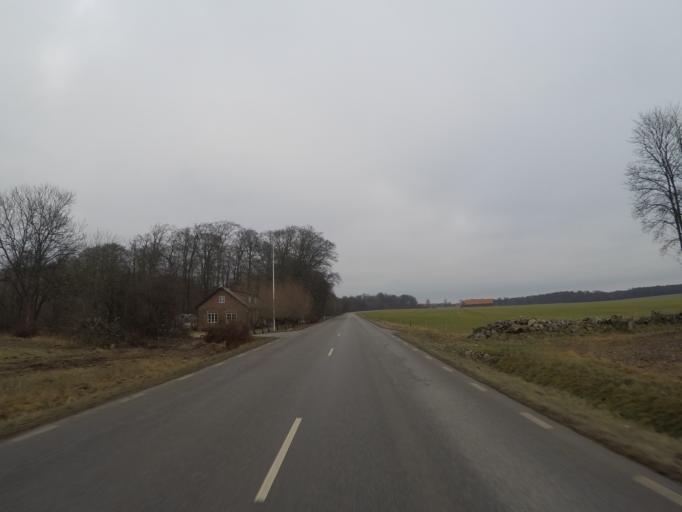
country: SE
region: Skane
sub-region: Hoors Kommun
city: Loberod
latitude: 55.7711
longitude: 13.4688
